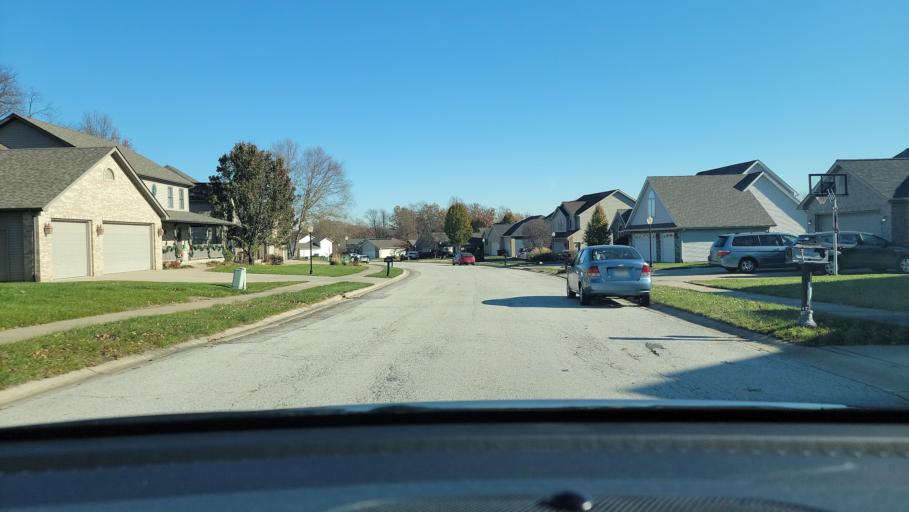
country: US
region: Indiana
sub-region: Porter County
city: Portage
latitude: 41.5876
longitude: -87.1503
